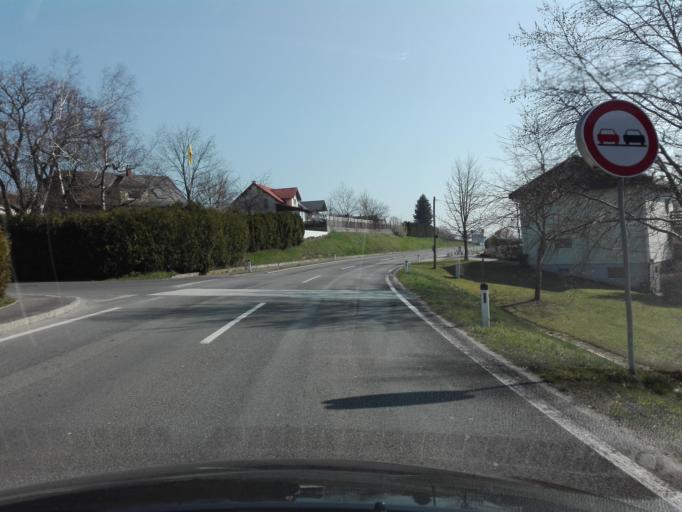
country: AT
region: Upper Austria
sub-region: Politischer Bezirk Urfahr-Umgebung
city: Gallneukirchen
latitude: 48.3400
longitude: 14.4080
